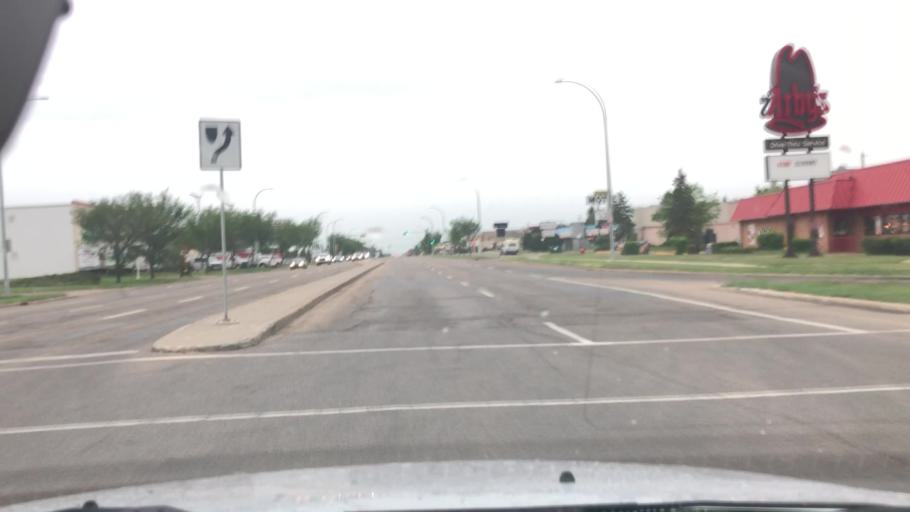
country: CA
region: Alberta
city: St. Albert
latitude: 53.5589
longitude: -113.5903
